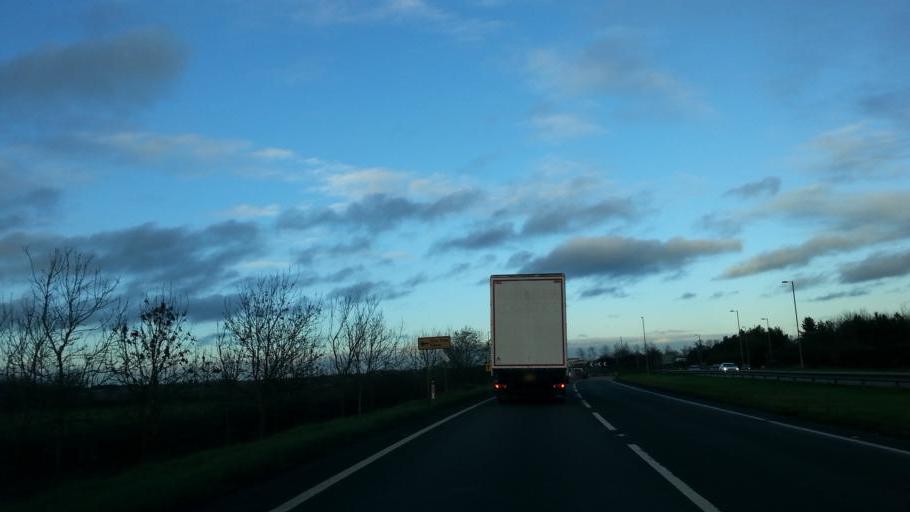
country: GB
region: England
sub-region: Northamptonshire
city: Brackley
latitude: 52.0109
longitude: -1.1586
